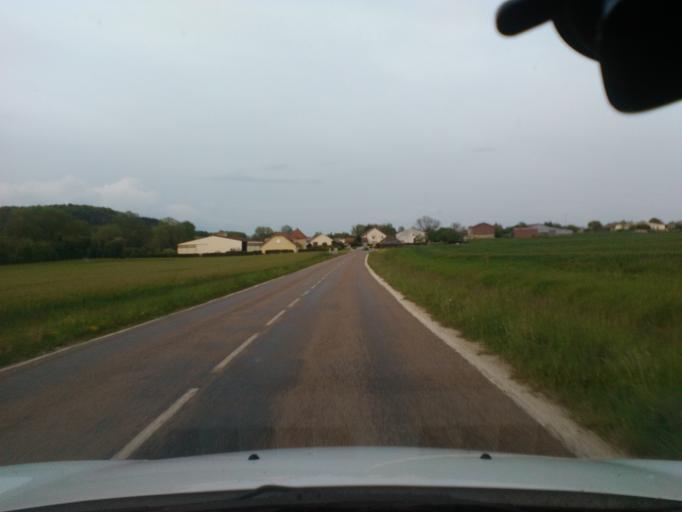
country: FR
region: Champagne-Ardenne
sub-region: Departement de la Haute-Marne
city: Bologne
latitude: 48.2175
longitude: 5.2392
